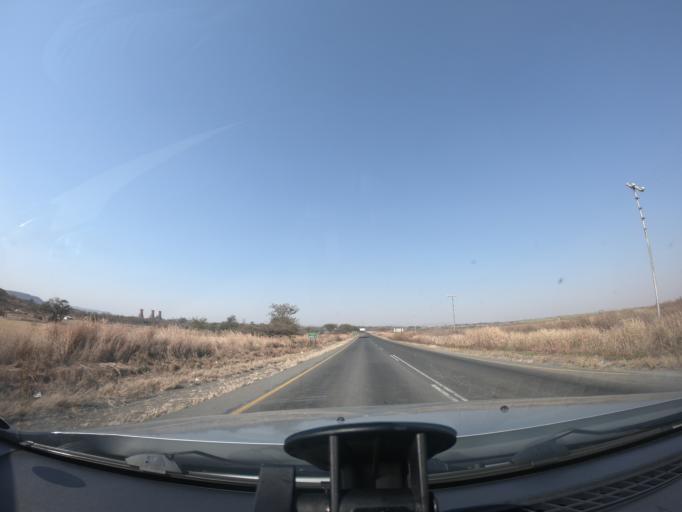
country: ZA
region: KwaZulu-Natal
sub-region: uThukela District Municipality
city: Ladysmith
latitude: -28.7295
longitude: 29.8105
